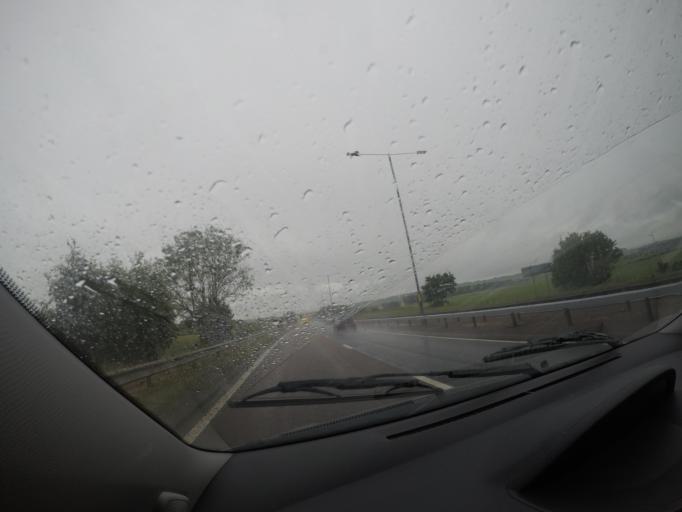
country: GB
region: Scotland
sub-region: Dundee City
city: Dundee
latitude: 56.5275
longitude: -2.9441
